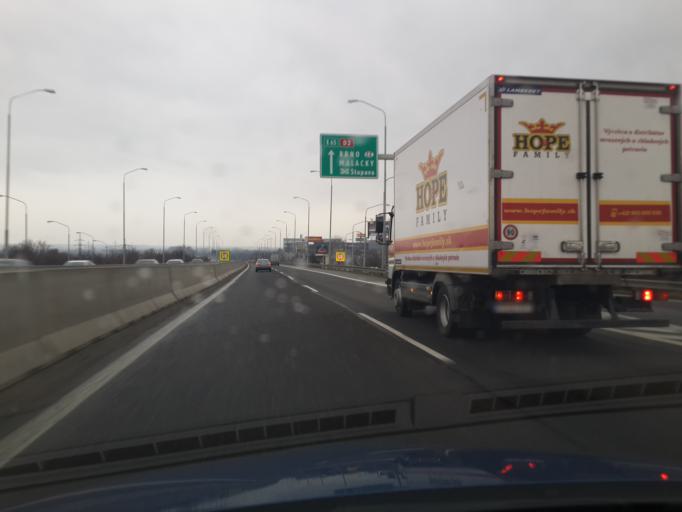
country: SK
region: Bratislavsky
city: Stupava
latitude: 48.2013
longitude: 17.0416
